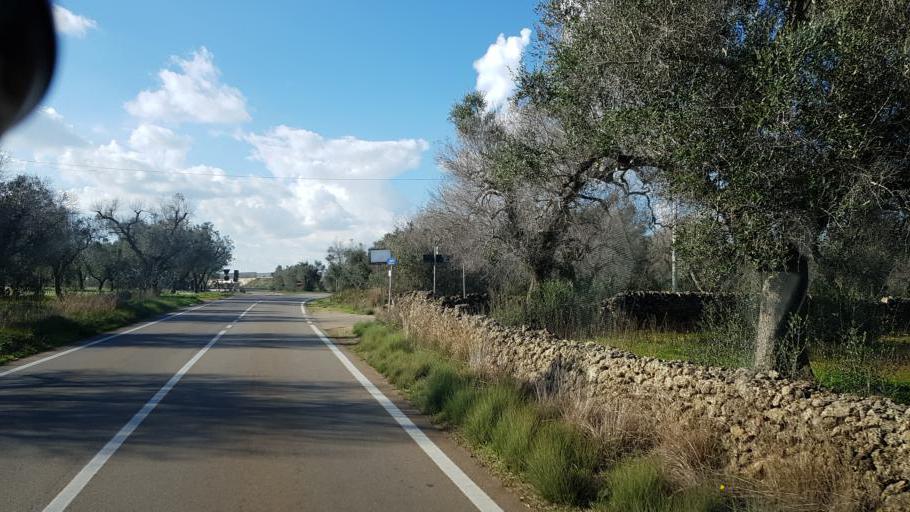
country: IT
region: Apulia
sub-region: Provincia di Lecce
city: Trepuzzi
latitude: 40.4401
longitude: 18.0831
